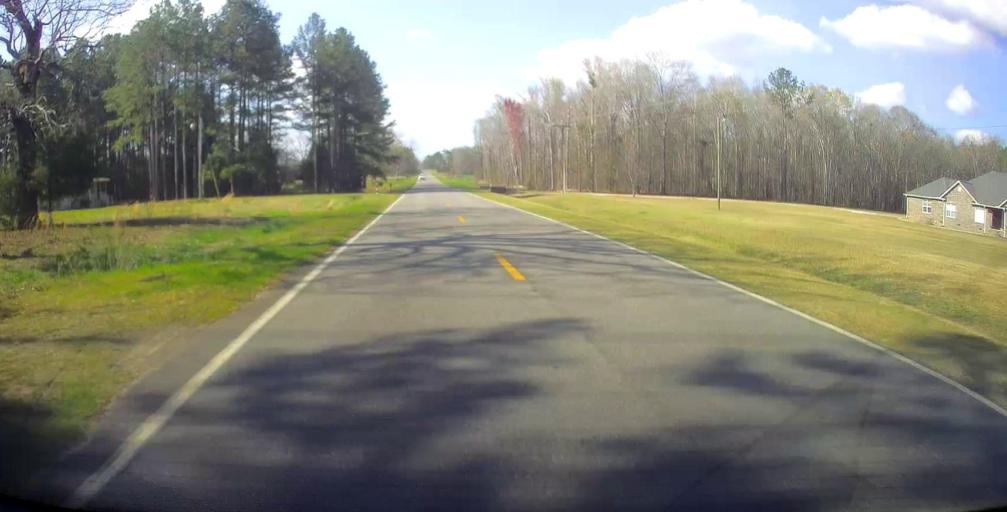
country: US
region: Georgia
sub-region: Laurens County
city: Dublin
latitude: 32.6127
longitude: -83.0821
